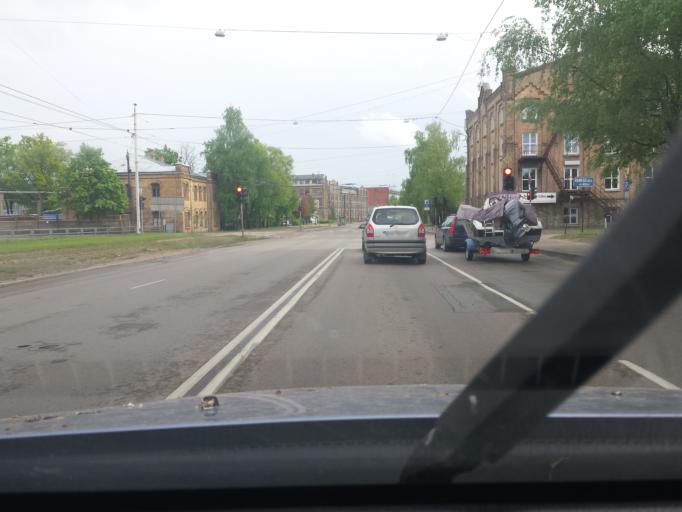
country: LV
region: Riga
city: Riga
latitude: 56.9891
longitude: 24.1217
